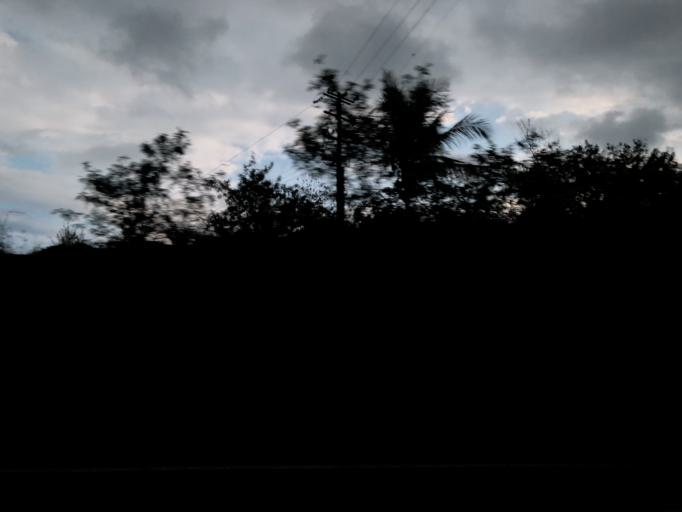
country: TW
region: Taiwan
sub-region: Taitung
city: Taitung
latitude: 22.8616
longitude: 121.2029
